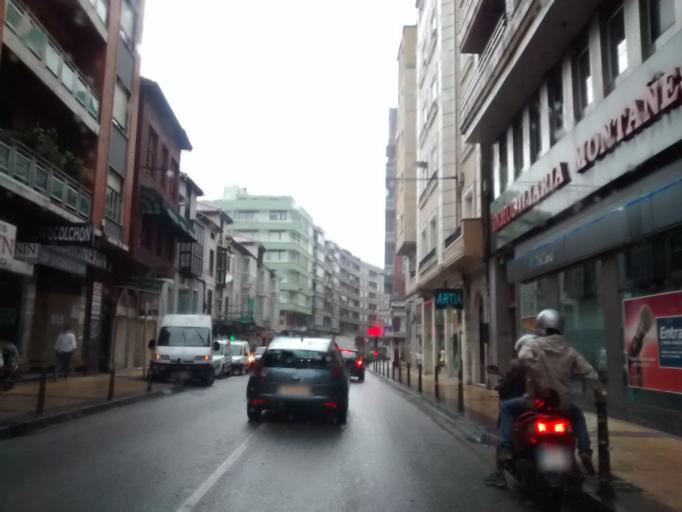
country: ES
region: Cantabria
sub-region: Provincia de Cantabria
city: Torrelavega
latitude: 43.3513
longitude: -4.0492
